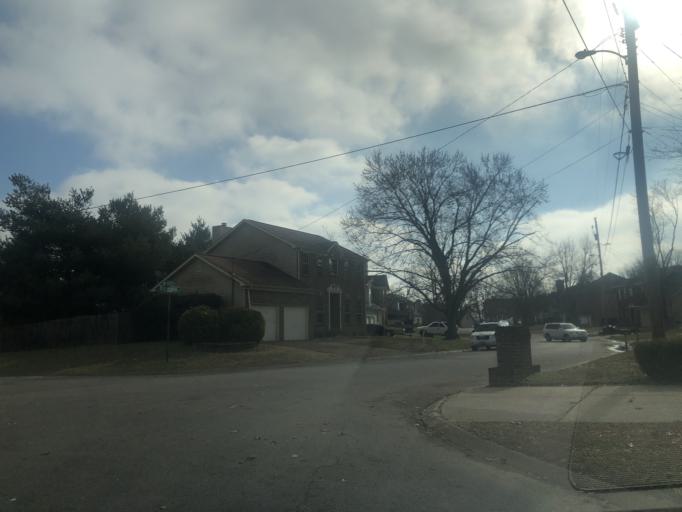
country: US
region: Tennessee
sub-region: Rutherford County
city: La Vergne
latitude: 36.0860
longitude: -86.6558
